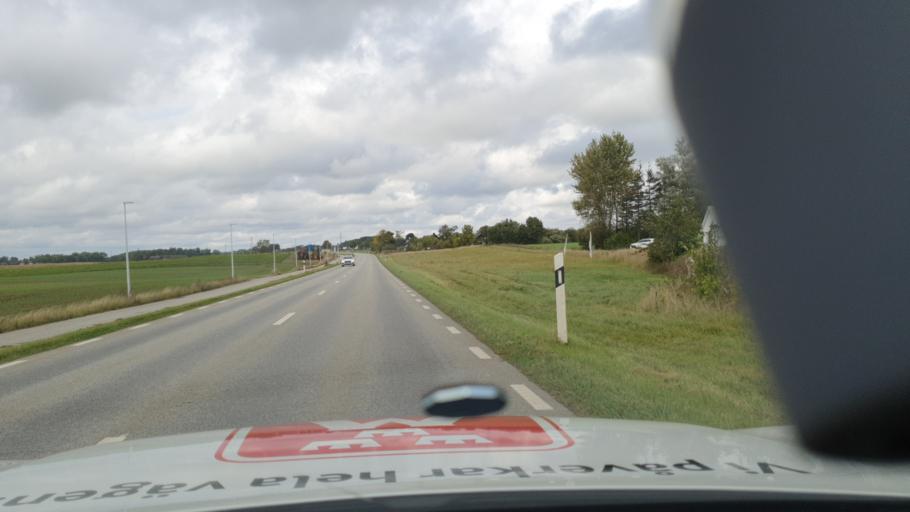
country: SE
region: Skane
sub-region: Malmo
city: Oxie
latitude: 55.5023
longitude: 13.1034
